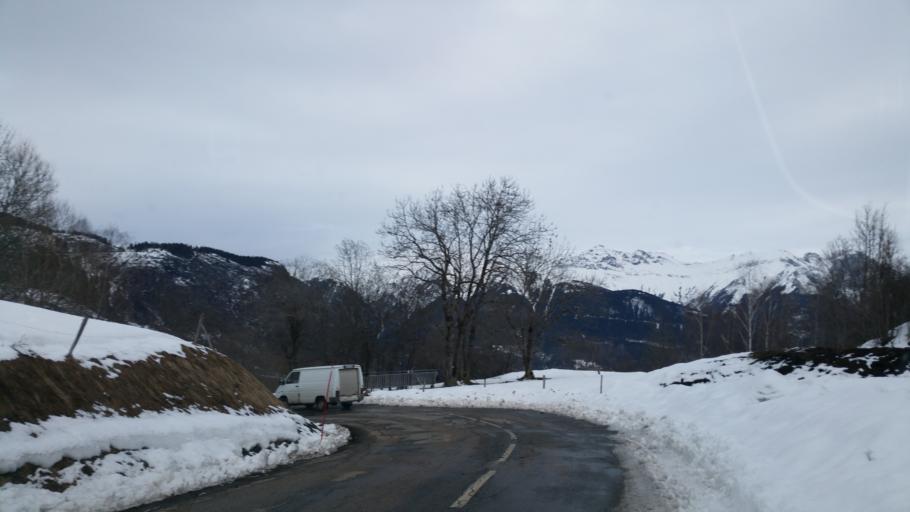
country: FR
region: Rhone-Alpes
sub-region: Departement de la Savoie
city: Saint-Jean-de-Maurienne
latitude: 45.2720
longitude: 6.3027
